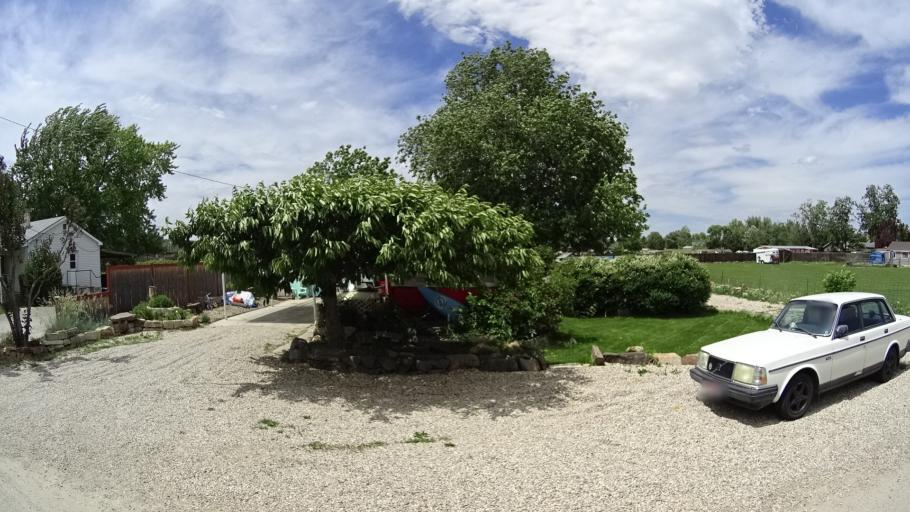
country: US
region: Idaho
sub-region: Ada County
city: Meridian
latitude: 43.6278
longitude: -116.3219
